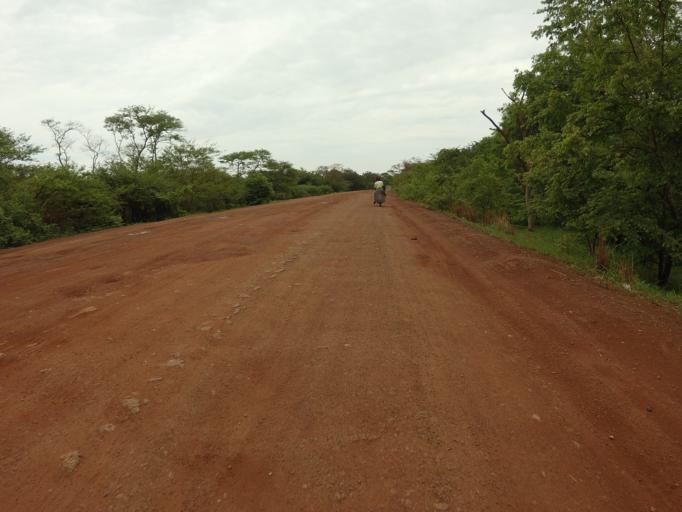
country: GH
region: Upper East
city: Bawku
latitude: 11.0009
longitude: -0.3932
